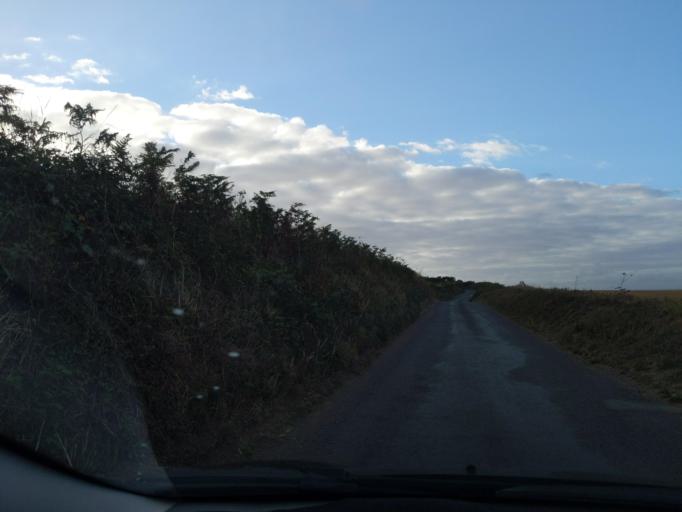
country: GB
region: England
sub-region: Devon
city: Salcombe
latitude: 50.2305
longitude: -3.8136
